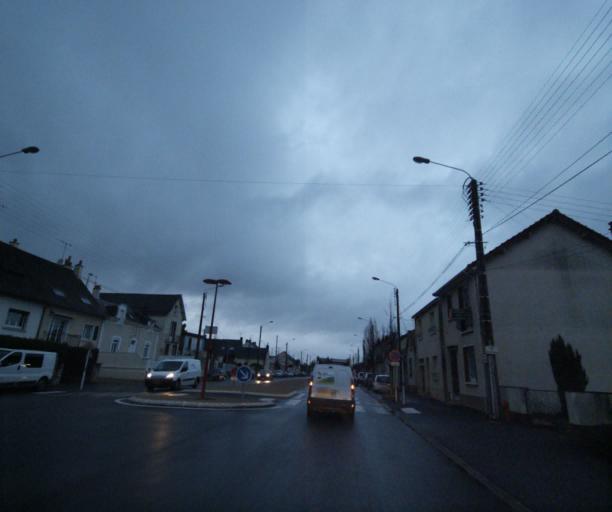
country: FR
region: Pays de la Loire
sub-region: Departement de la Sarthe
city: Coulaines
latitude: 48.0212
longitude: 0.1837
